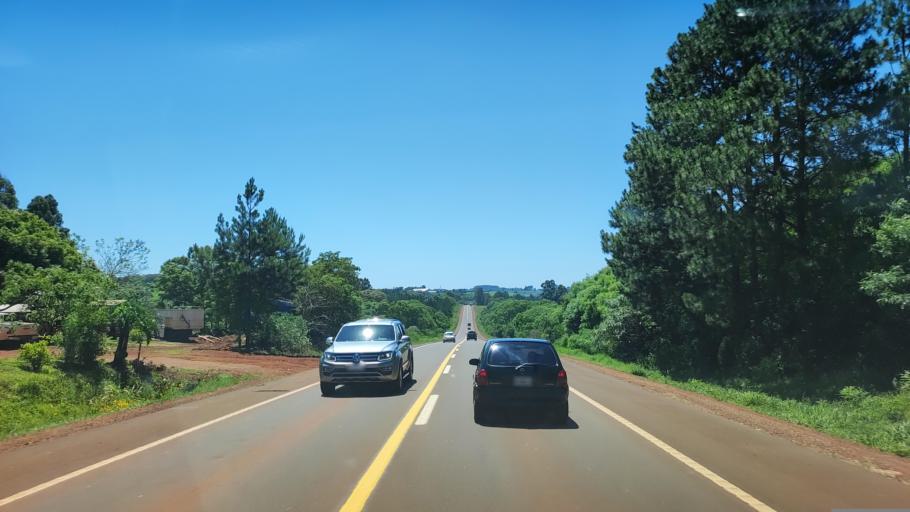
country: AR
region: Misiones
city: Aristobulo del Valle
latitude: -27.0854
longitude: -54.8007
